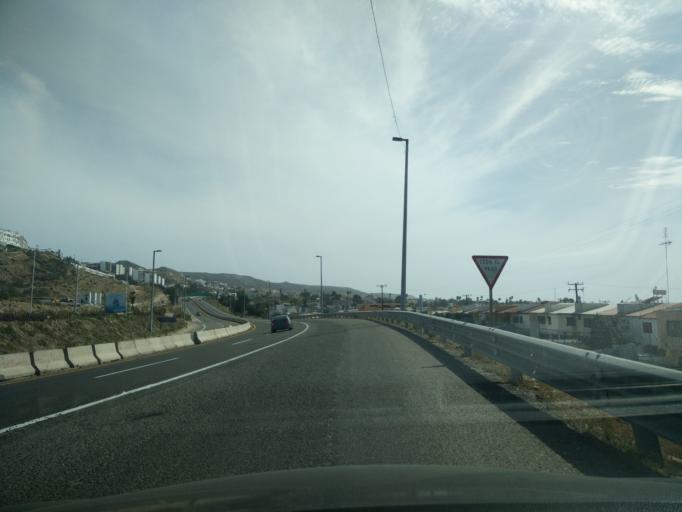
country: US
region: California
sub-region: San Diego County
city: Imperial Beach
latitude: 32.5328
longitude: -117.1089
